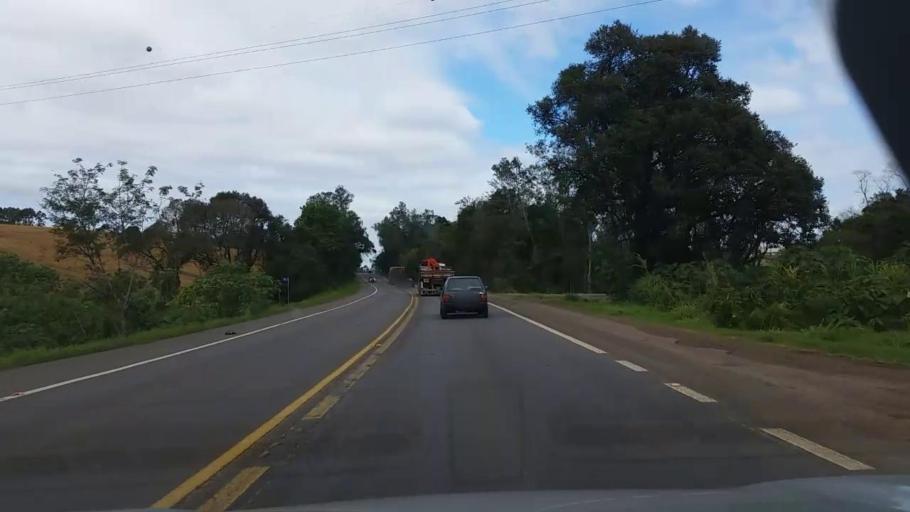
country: BR
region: Rio Grande do Sul
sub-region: Lajeado
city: Lajeado
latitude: -29.4164
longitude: -52.0248
